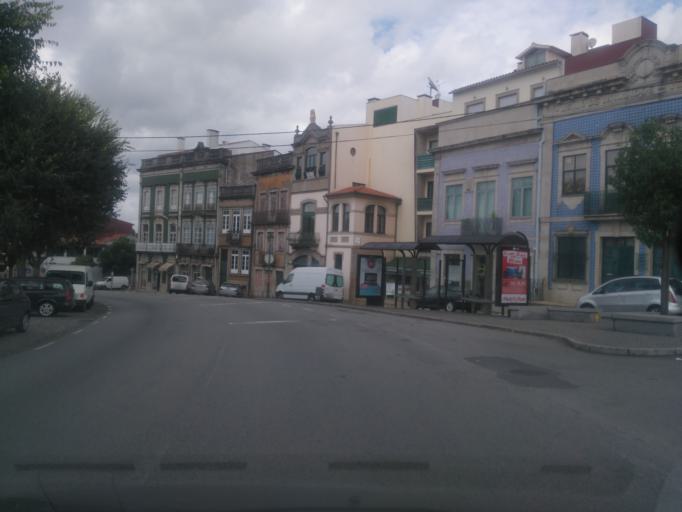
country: PT
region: Braga
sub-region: Braga
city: Braga
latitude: 41.5564
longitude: -8.4418
